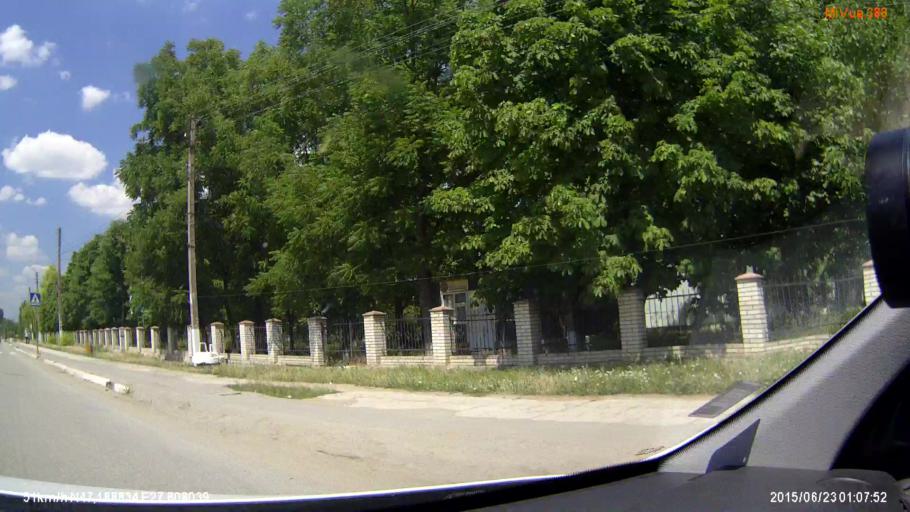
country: MD
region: Ungheni
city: Ungheni
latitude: 47.1887
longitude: 27.8081
